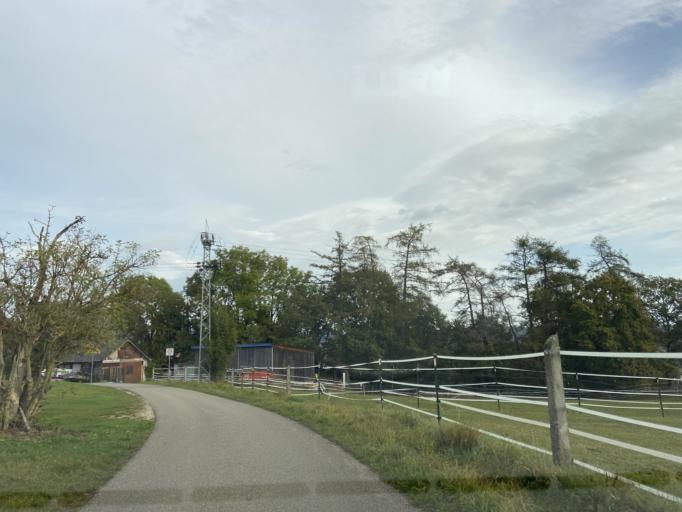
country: DE
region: Baden-Wuerttemberg
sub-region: Tuebingen Region
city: Bingen
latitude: 48.1066
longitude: 9.2749
